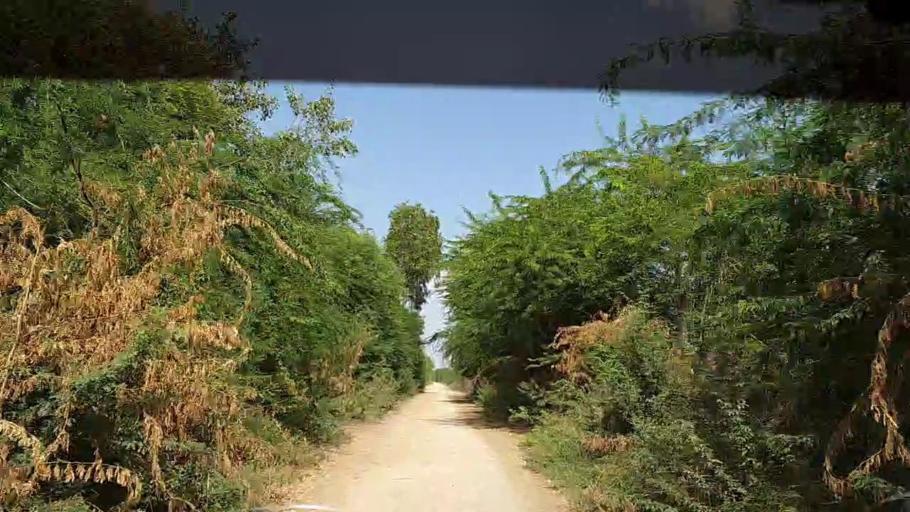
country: PK
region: Sindh
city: Badin
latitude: 24.5866
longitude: 68.7927
